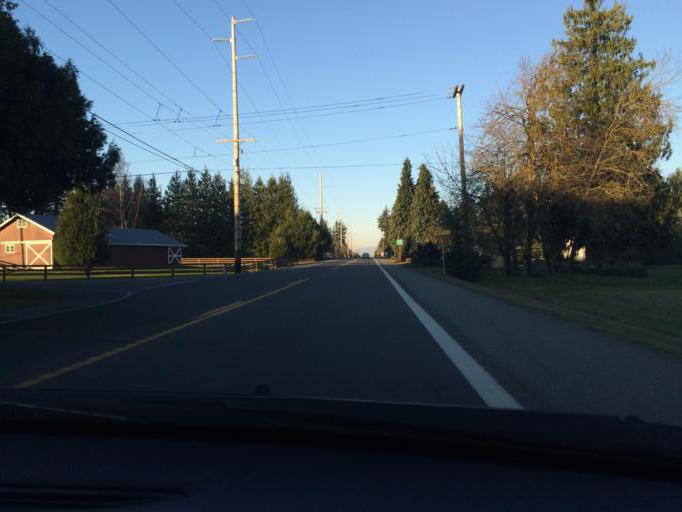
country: US
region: Washington
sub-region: Whatcom County
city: Lynden
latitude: 48.9096
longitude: -122.4420
